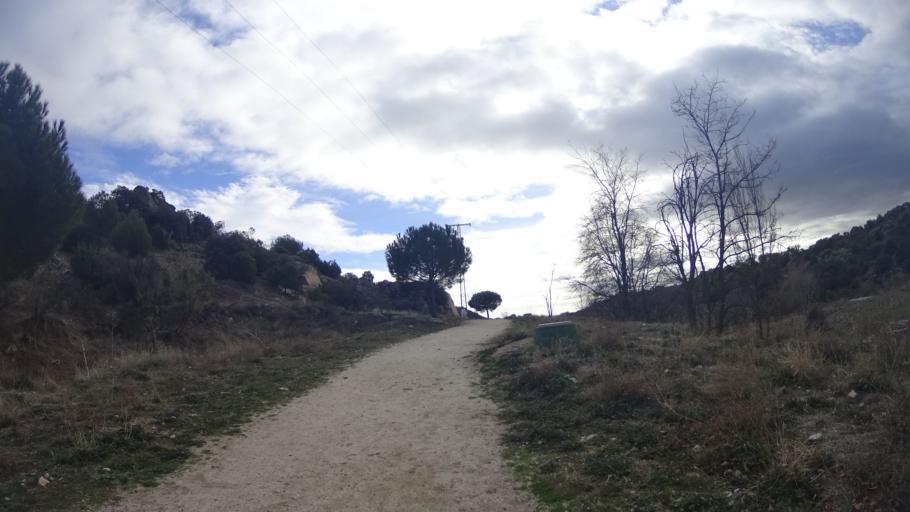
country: ES
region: Madrid
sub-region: Provincia de Madrid
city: Torrelodones
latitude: 40.5713
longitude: -3.9297
